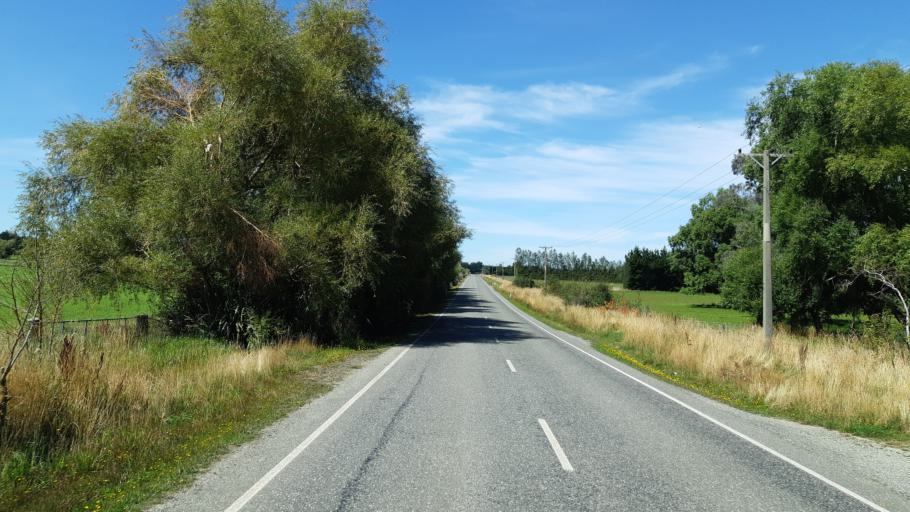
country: NZ
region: Southland
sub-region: Gore District
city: Gore
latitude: -46.0040
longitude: 168.9049
